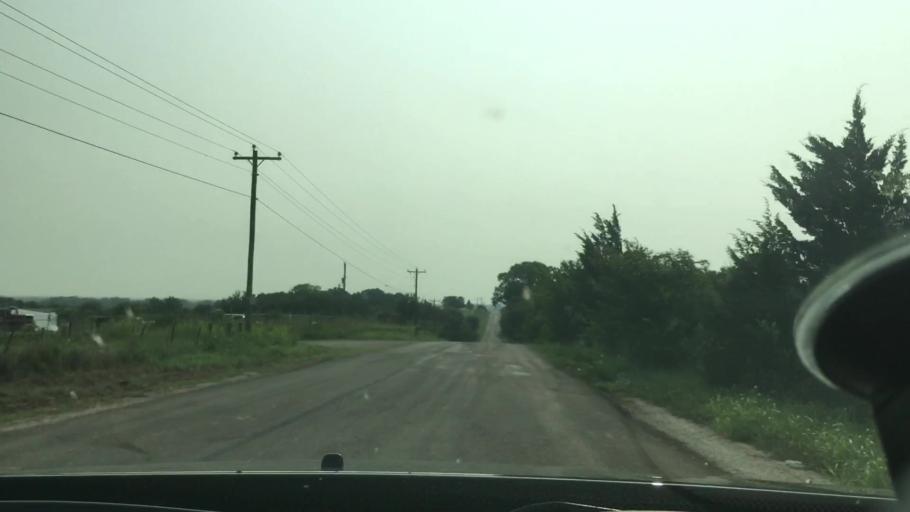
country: US
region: Oklahoma
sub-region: Garvin County
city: Lindsay
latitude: 34.8120
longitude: -97.6459
